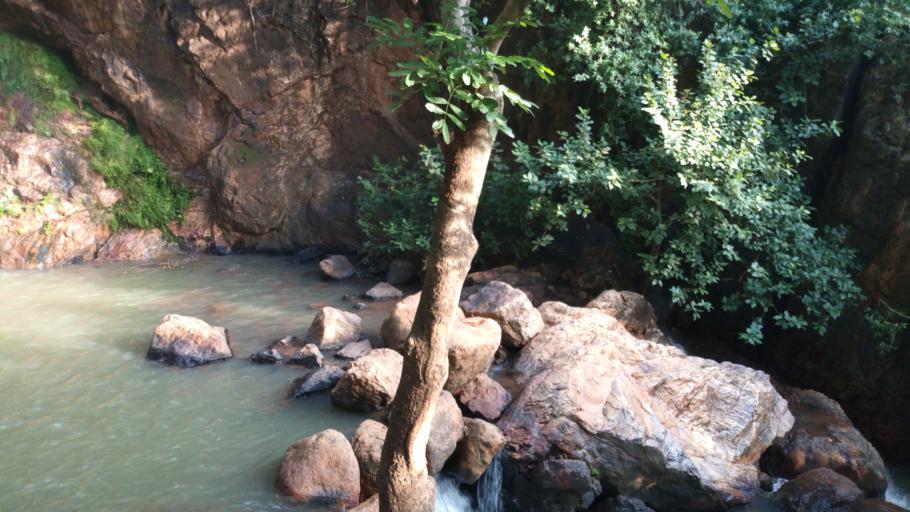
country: BJ
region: Atakora
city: Tanguieta
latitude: 10.6145
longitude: 1.2837
